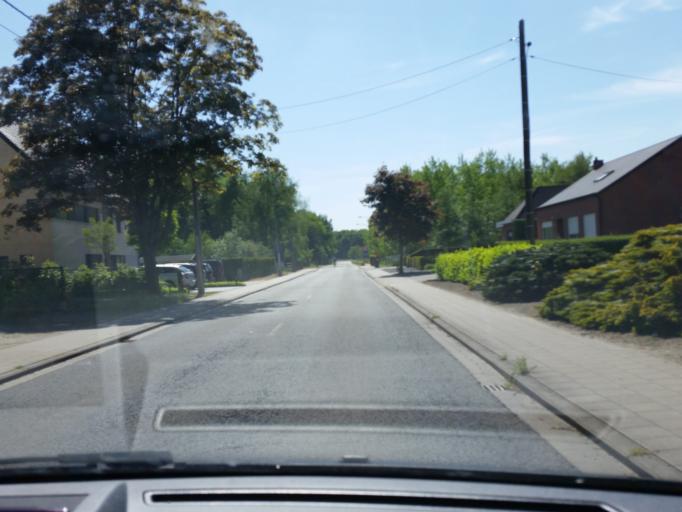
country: BE
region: Flanders
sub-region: Provincie Antwerpen
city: Bonheiden
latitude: 51.0200
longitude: 4.5359
